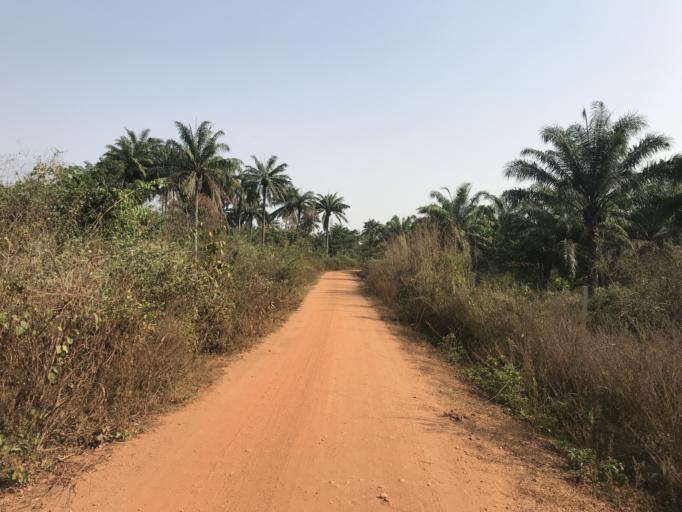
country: NG
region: Osun
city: Olupona
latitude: 7.6123
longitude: 4.1493
